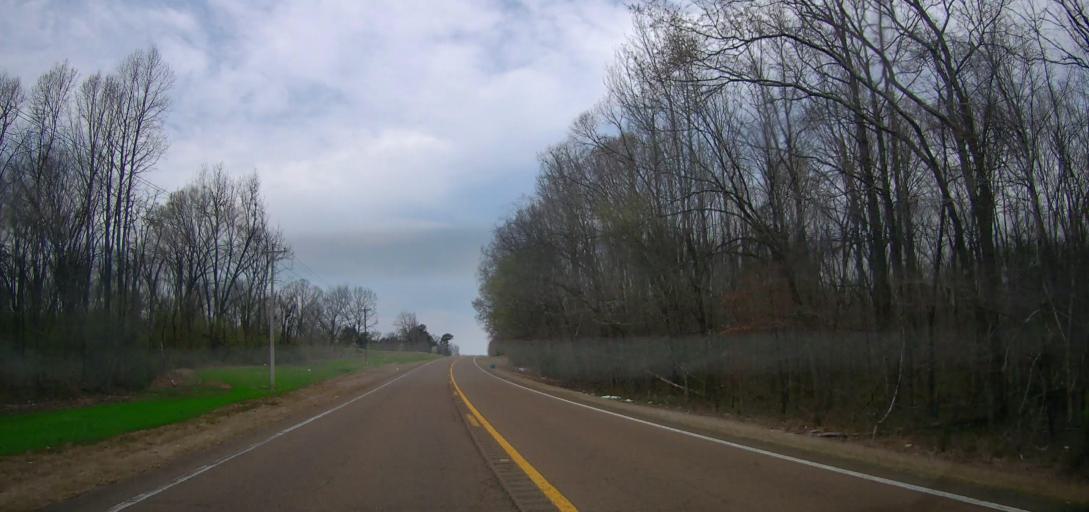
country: US
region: Mississippi
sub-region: Marshall County
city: Byhalia
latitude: 34.8489
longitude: -89.6278
